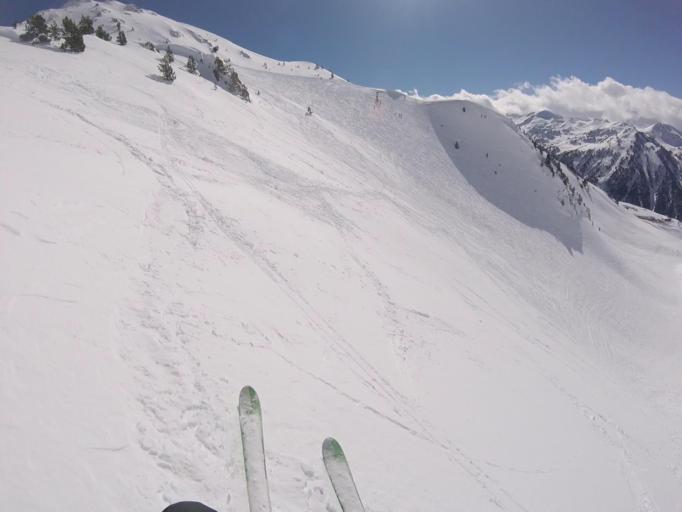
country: ES
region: Catalonia
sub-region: Provincia de Lleida
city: Espot
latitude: 42.6712
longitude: 0.9873
